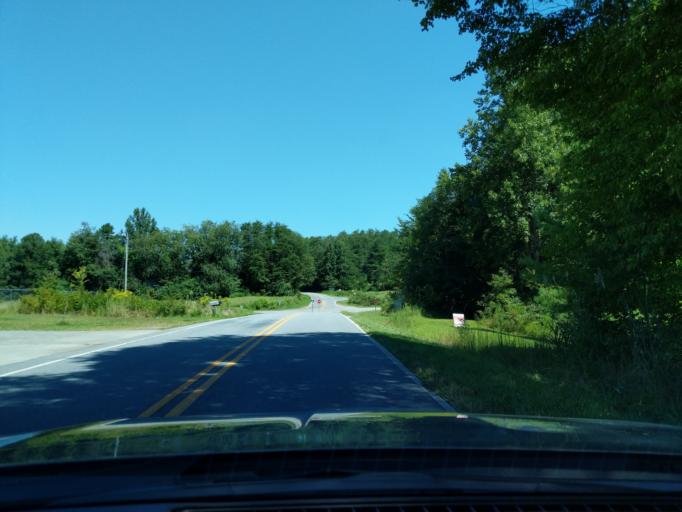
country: US
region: North Carolina
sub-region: Clay County
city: Hayesville
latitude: 35.0317
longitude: -83.7342
